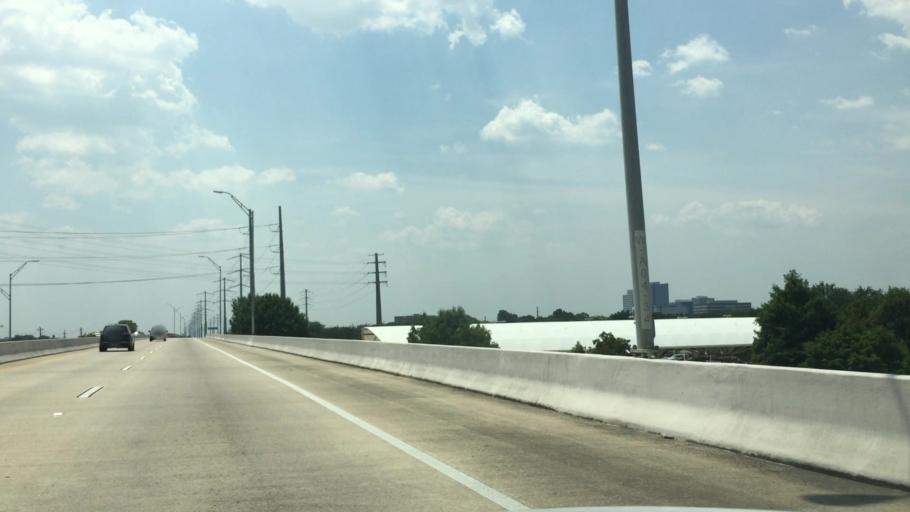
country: US
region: Texas
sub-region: Harris County
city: Piney Point Village
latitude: 29.7200
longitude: -95.5361
